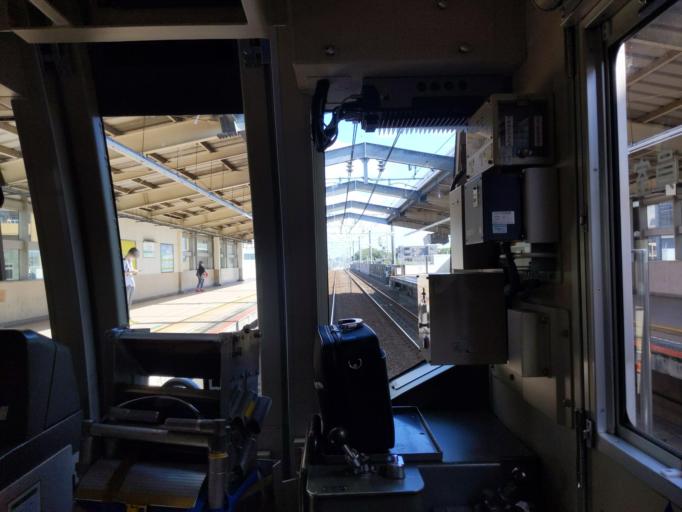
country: JP
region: Chiba
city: Shiroi
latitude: 35.7280
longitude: 140.1028
